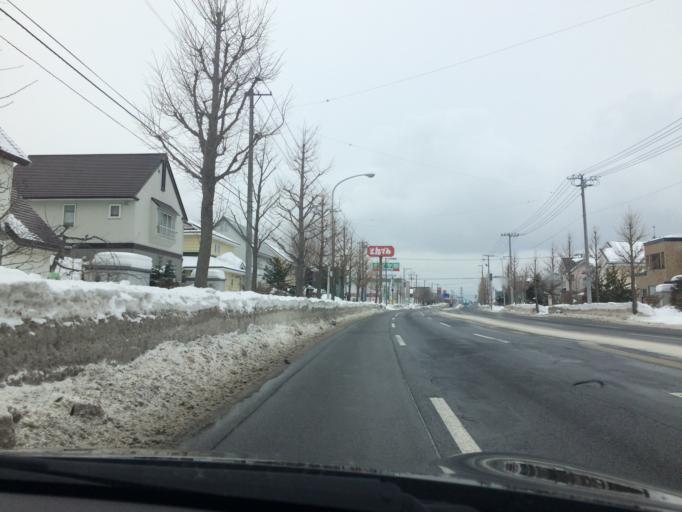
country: JP
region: Hokkaido
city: Ebetsu
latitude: 43.0576
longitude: 141.4737
